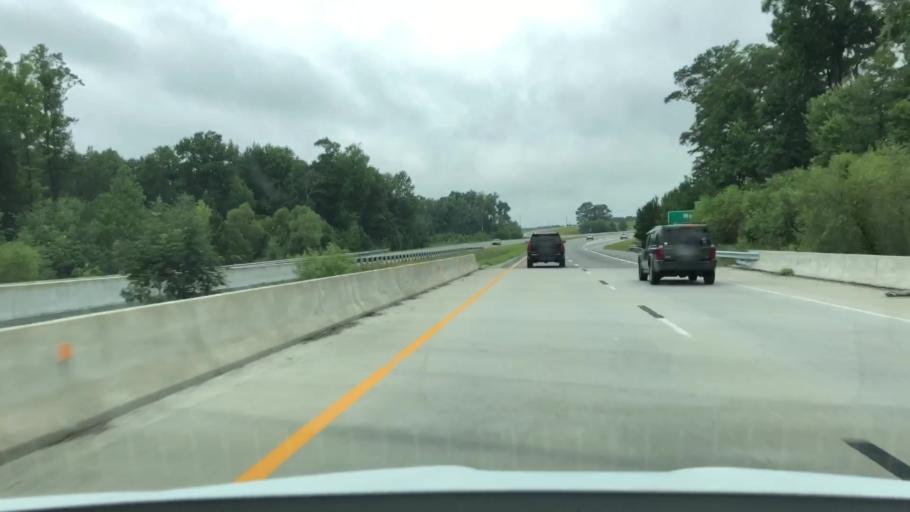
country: US
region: North Carolina
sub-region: Wayne County
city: Goldsboro
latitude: 35.4180
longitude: -77.9276
